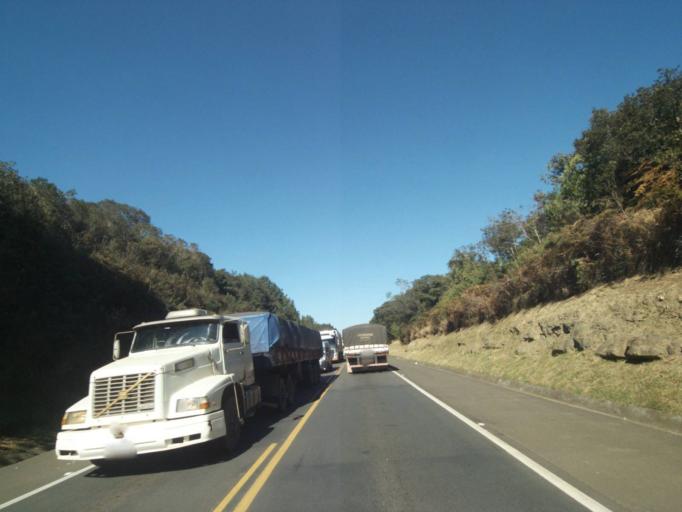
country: BR
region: Parana
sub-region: Tibagi
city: Tibagi
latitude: -24.6788
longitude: -50.5965
